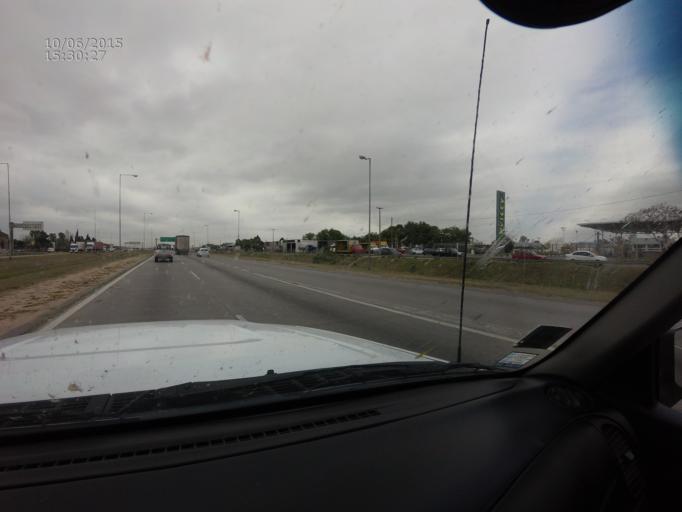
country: AR
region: Cordoba
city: Malvinas Argentinas
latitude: -31.3841
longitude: -64.1265
